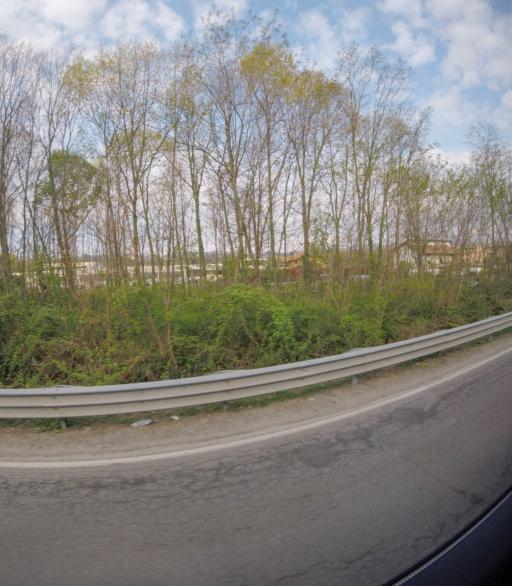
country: IT
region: Piedmont
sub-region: Provincia di Novara
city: Briga Novarese
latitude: 45.7287
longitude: 8.4442
